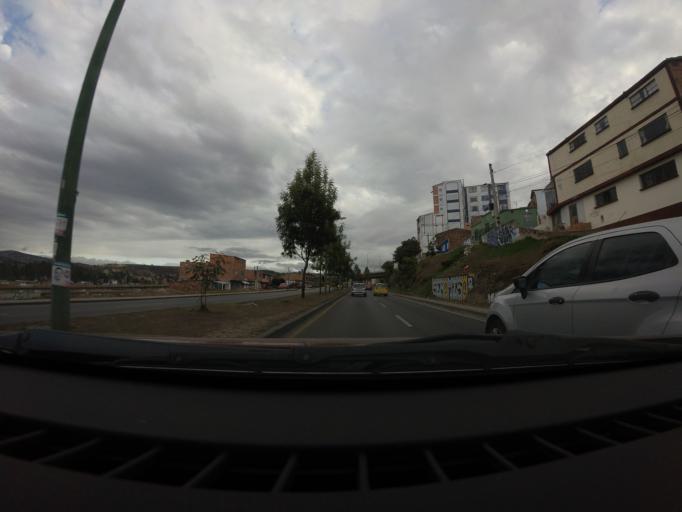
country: CO
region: Boyaca
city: Tunja
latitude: 5.5356
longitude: -73.3555
